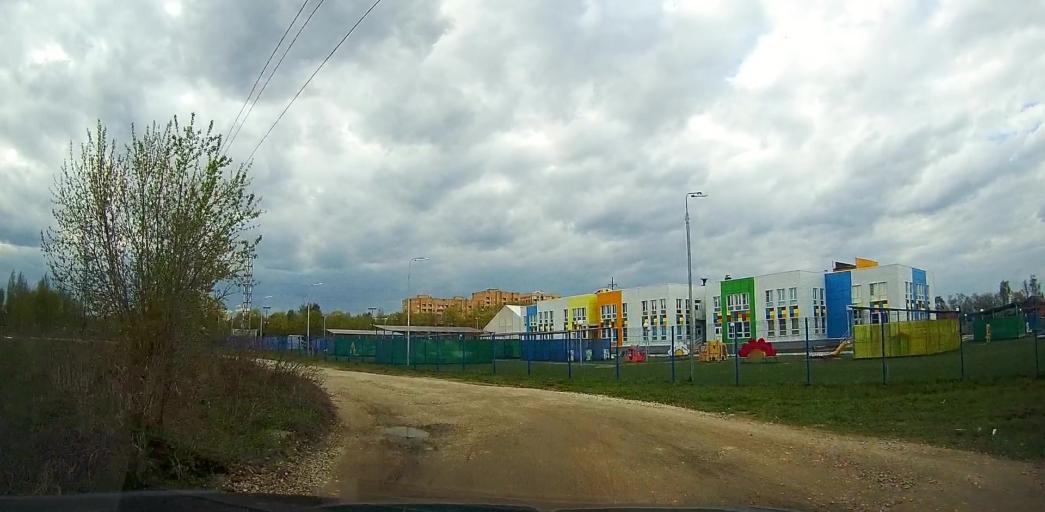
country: RU
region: Moskovskaya
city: Pavlovskiy Posad
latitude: 55.7800
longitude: 38.6300
